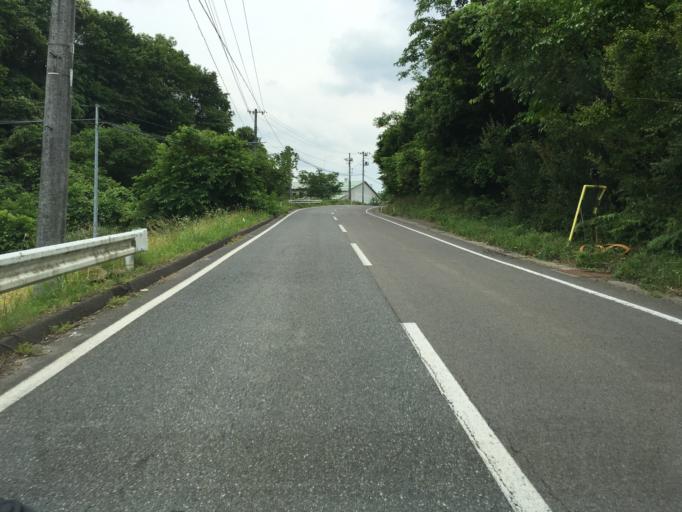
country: JP
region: Fukushima
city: Yanagawamachi-saiwaicho
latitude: 37.7450
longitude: 140.6388
